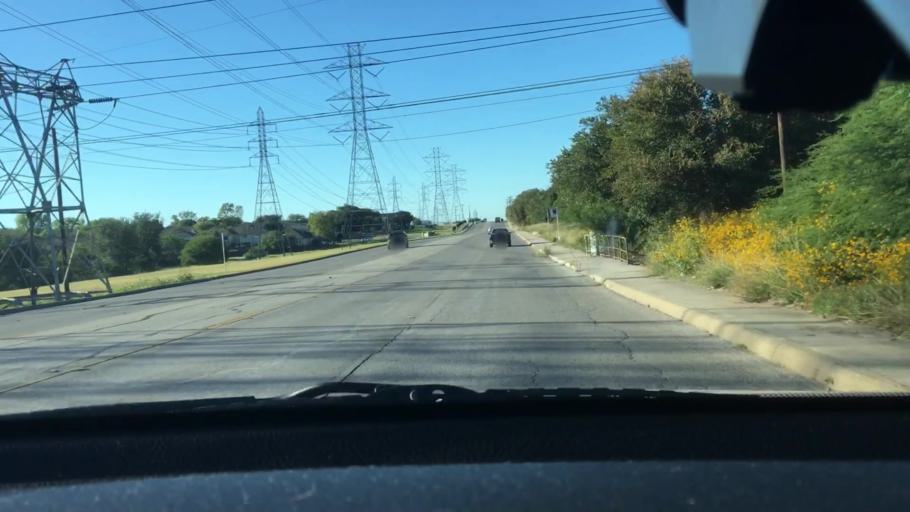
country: US
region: Texas
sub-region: Bexar County
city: Windcrest
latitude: 29.5371
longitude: -98.3610
